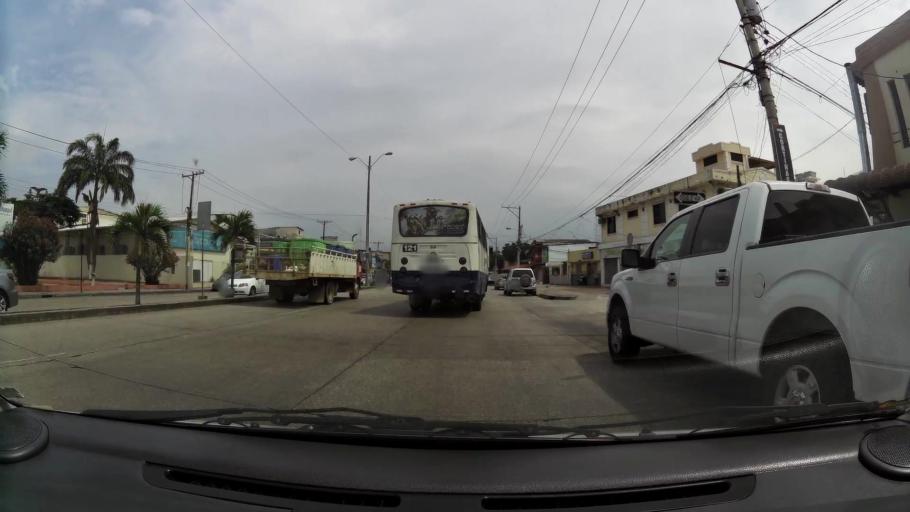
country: EC
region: Guayas
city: Eloy Alfaro
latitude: -2.1422
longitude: -79.8903
